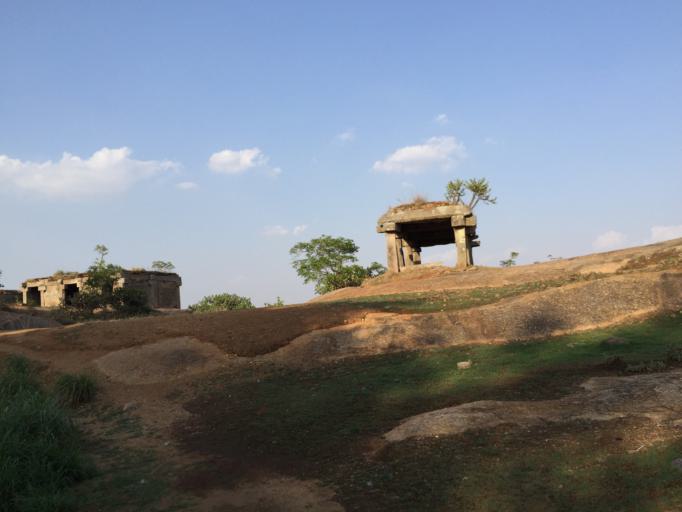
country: IN
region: Karnataka
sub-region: Ramanagara
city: Magadi
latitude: 12.9209
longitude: 77.2938
